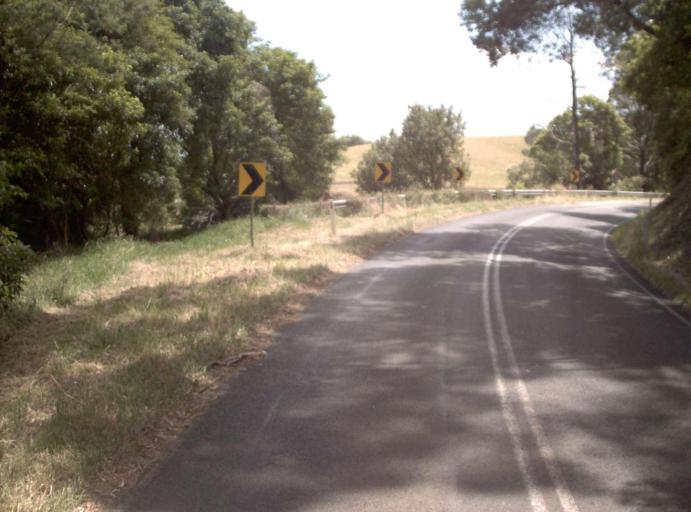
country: AU
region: Victoria
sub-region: Baw Baw
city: Warragul
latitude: -38.2673
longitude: 145.8923
